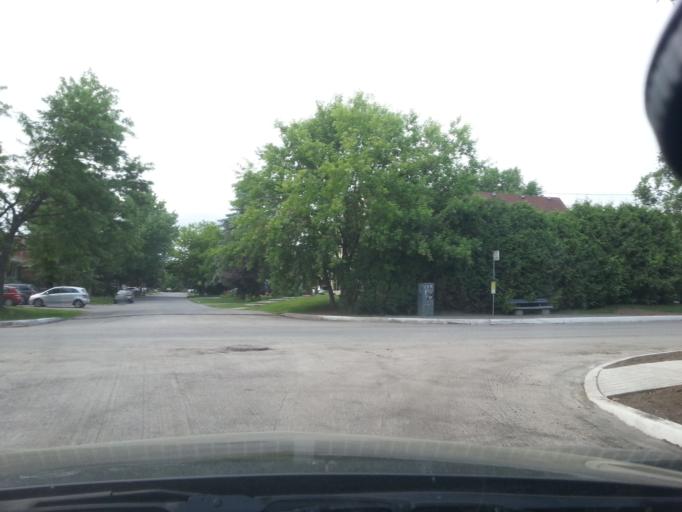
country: CA
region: Ontario
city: Ottawa
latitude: 45.3829
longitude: -75.7543
